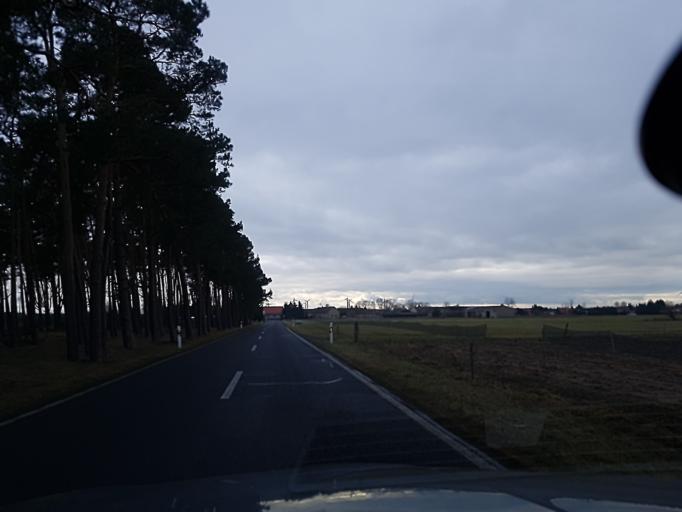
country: DE
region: Brandenburg
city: Bad Liebenwerda
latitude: 51.5519
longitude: 13.3370
